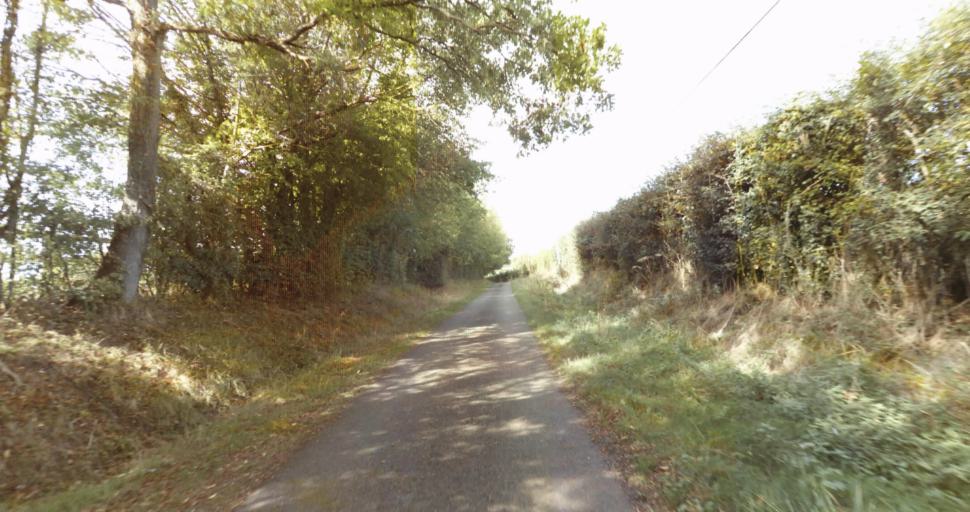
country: FR
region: Lower Normandy
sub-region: Departement de l'Orne
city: Sees
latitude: 48.7106
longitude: 0.1758
